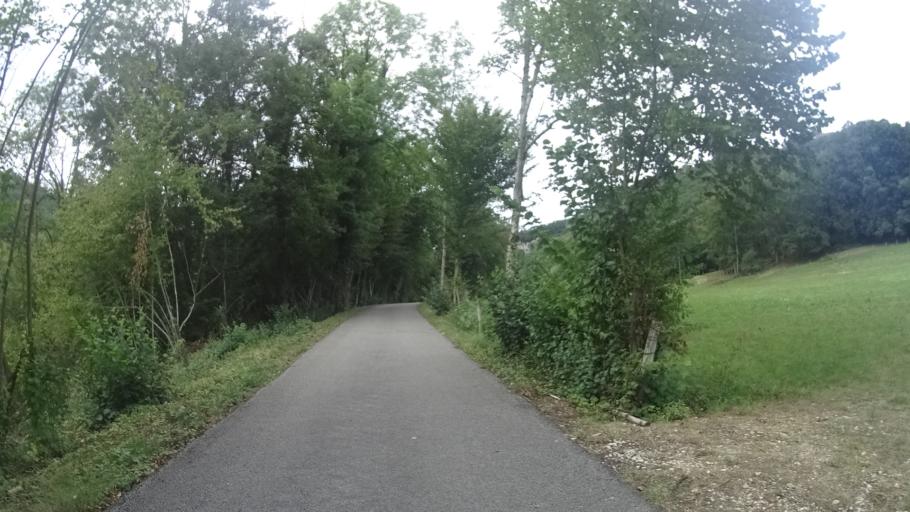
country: FR
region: Franche-Comte
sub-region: Departement du Doubs
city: Baume-les-Dames
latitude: 47.3360
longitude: 6.3476
